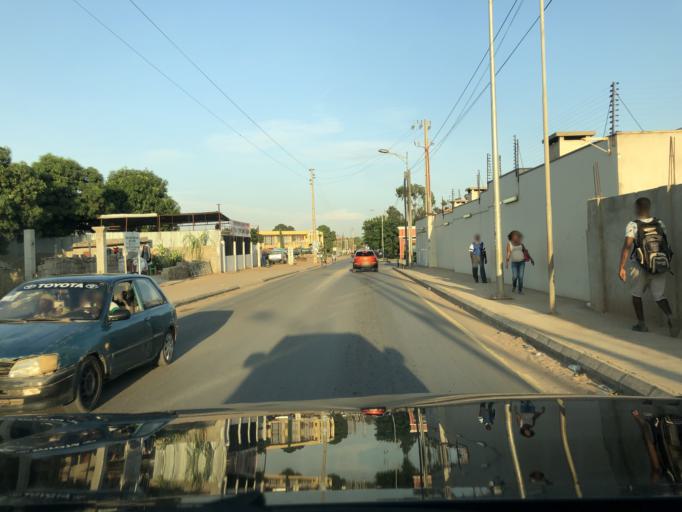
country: AO
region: Luanda
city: Luanda
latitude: -8.9483
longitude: 13.1671
